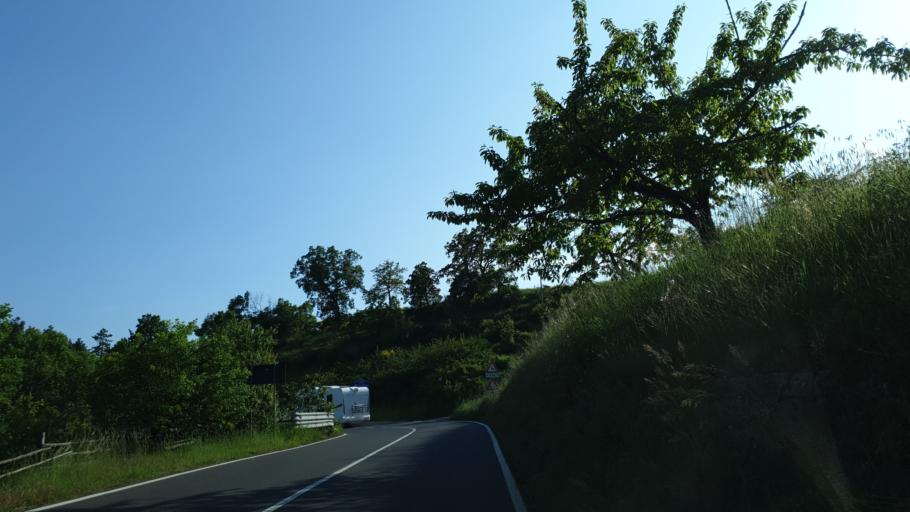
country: IT
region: Tuscany
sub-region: Province of Arezzo
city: Stia
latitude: 43.7760
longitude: 11.6917
